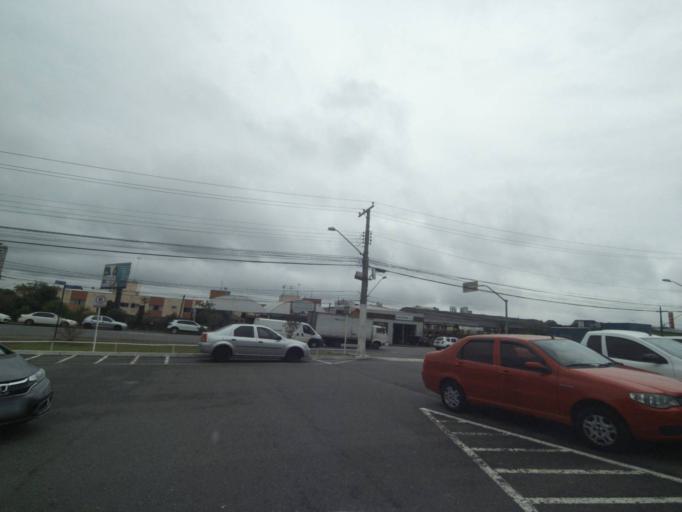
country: BR
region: Parana
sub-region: Curitiba
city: Curitiba
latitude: -25.4333
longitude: -49.3110
